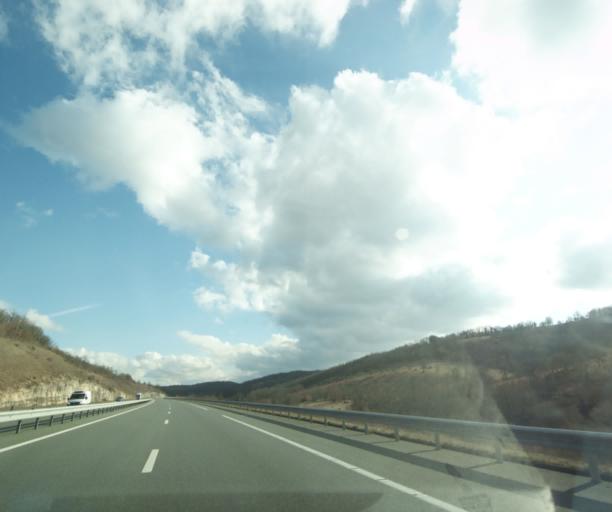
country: FR
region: Midi-Pyrenees
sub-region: Departement du Lot
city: Le Vigan
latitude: 44.7463
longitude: 1.5461
